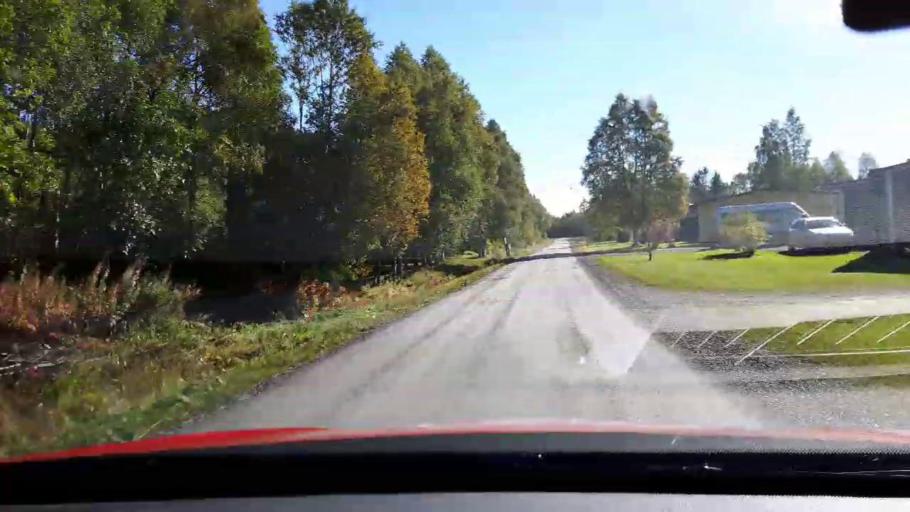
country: NO
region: Nord-Trondelag
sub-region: Lierne
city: Sandvika
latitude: 64.6486
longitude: 13.7545
